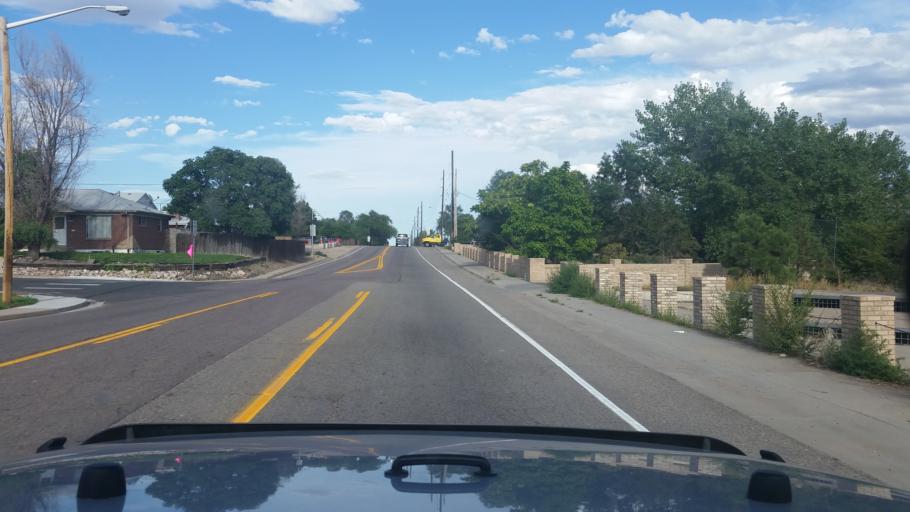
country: US
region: Colorado
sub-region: Adams County
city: Twin Lakes
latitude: 39.8236
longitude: -105.0025
